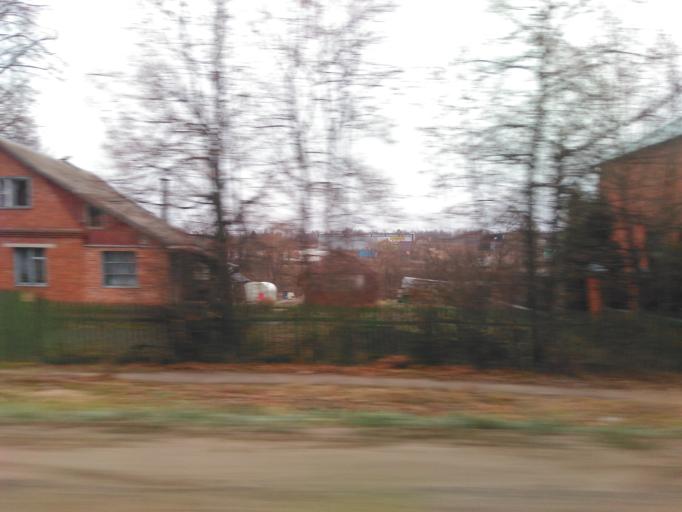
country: RU
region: Moskovskaya
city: Sofrino
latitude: 56.1158
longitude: 37.9600
